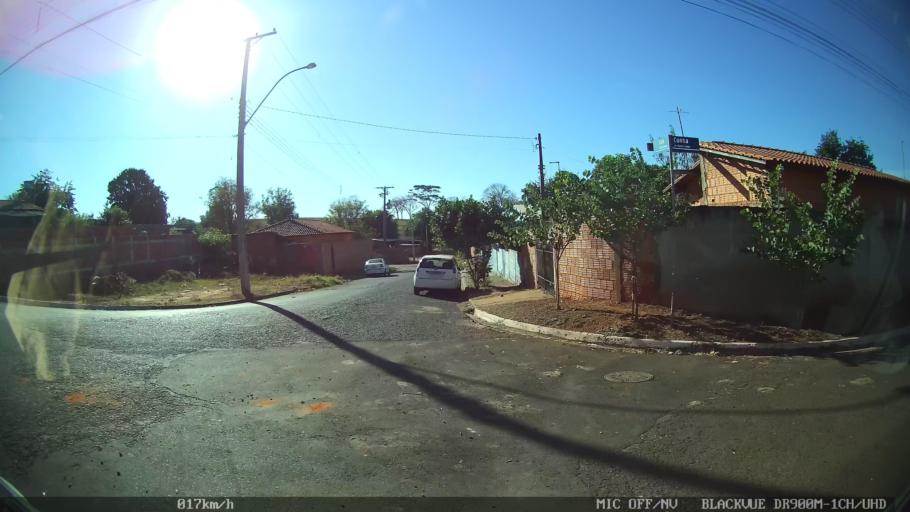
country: BR
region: Sao Paulo
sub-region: Olimpia
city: Olimpia
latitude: -20.7239
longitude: -48.8889
